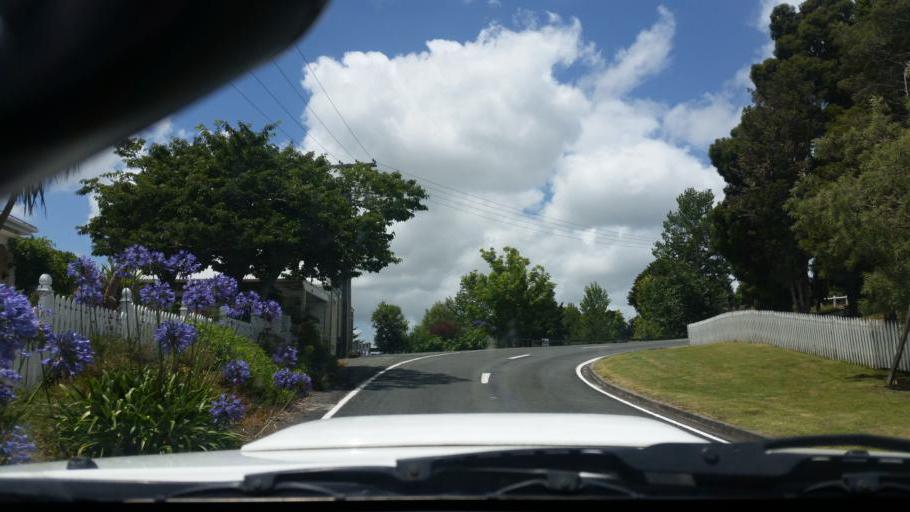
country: NZ
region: Northland
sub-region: Whangarei
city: Ruakaka
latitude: -36.0968
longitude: 174.2418
